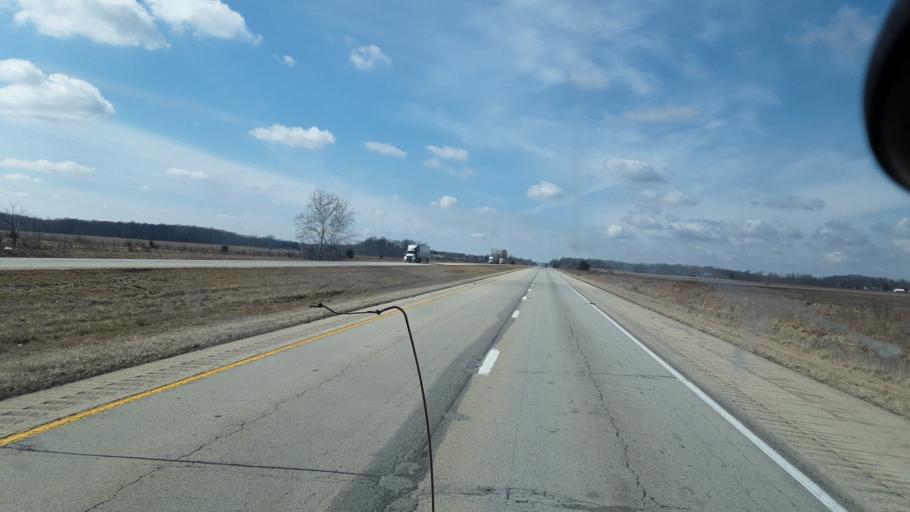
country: US
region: Illinois
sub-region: Effingham County
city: Teutopolis
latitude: 39.1585
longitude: -88.4520
